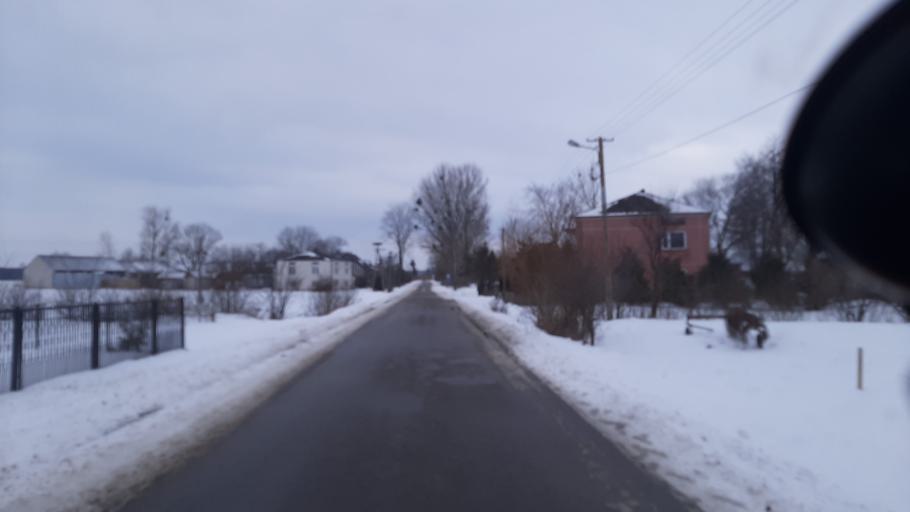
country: PL
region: Lublin Voivodeship
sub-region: Powiat lubartowski
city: Abramow
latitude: 51.4424
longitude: 22.2843
